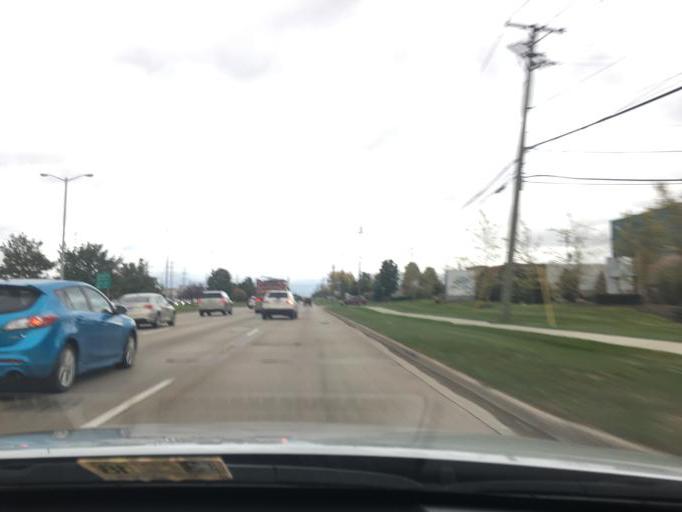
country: US
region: Michigan
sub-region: Macomb County
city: Sterling Heights
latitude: 42.5668
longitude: -83.0490
